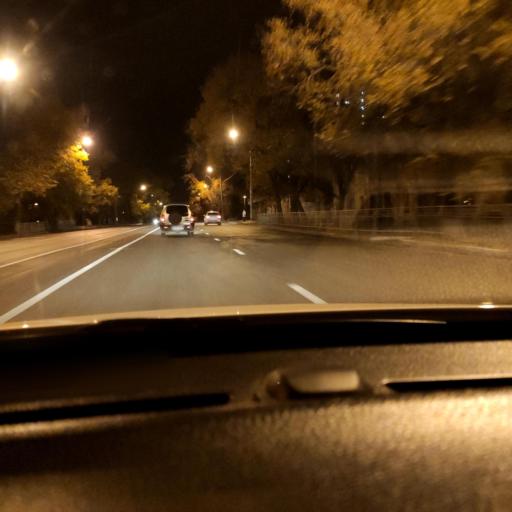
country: RU
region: Voronezj
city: Maslovka
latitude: 51.6191
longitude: 39.2504
